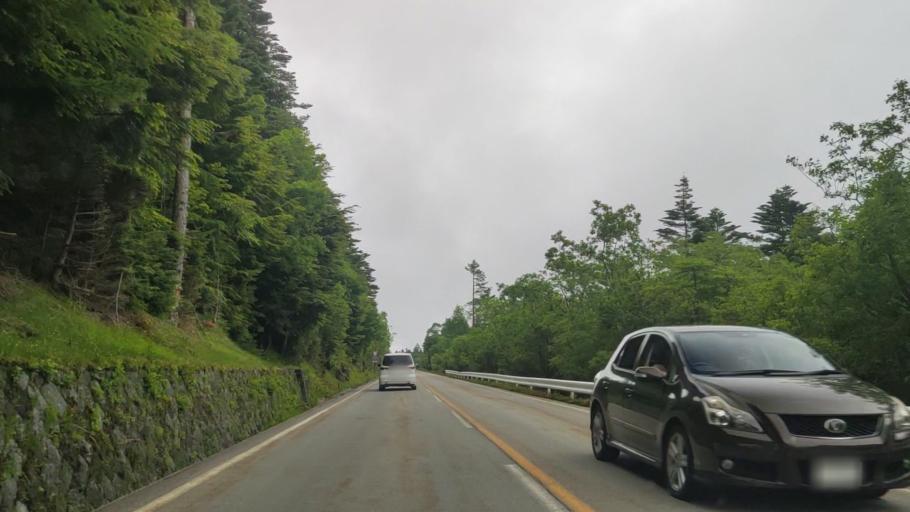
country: JP
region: Yamanashi
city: Fujikawaguchiko
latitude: 35.3941
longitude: 138.6916
